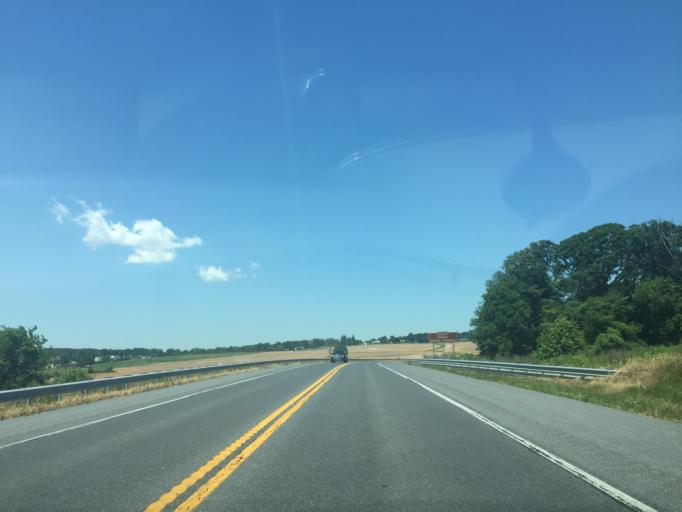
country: US
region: Maryland
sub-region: Carroll County
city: Hampstead
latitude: 39.5853
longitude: -76.8503
